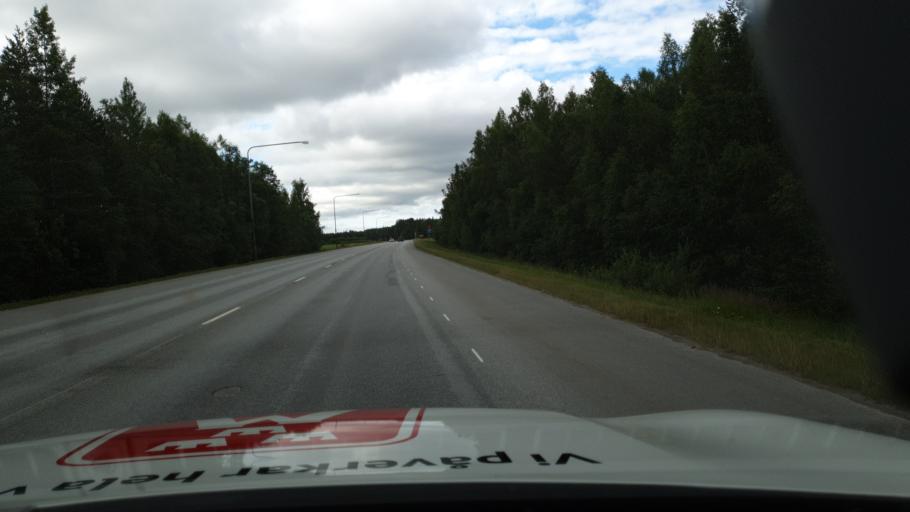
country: SE
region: Vaesterbotten
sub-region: Umea Kommun
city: Roback
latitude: 63.7808
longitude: 20.2038
